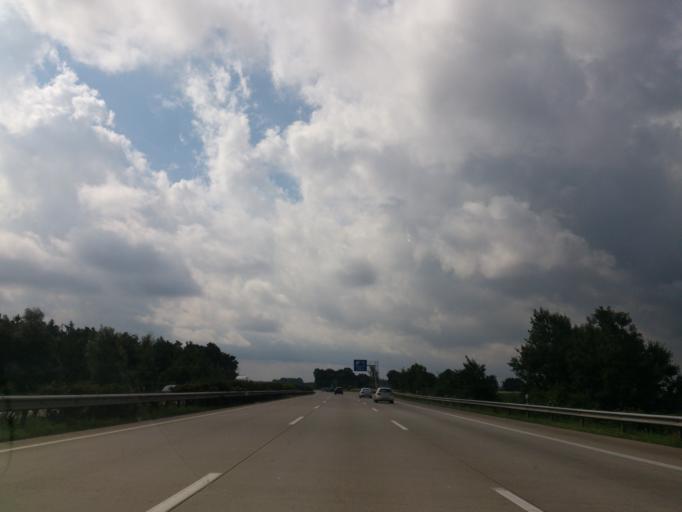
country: DE
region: Lower Saxony
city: Egestorf
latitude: 53.2034
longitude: 10.0790
